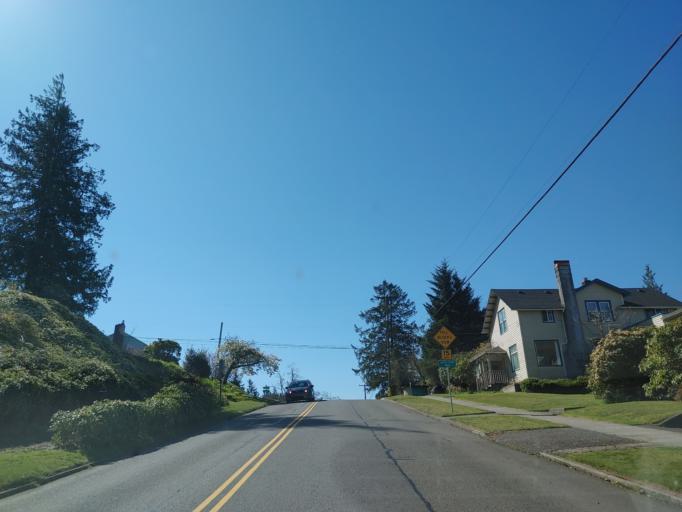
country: US
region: Oregon
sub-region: Clatsop County
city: Astoria
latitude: 46.1827
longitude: -123.8265
